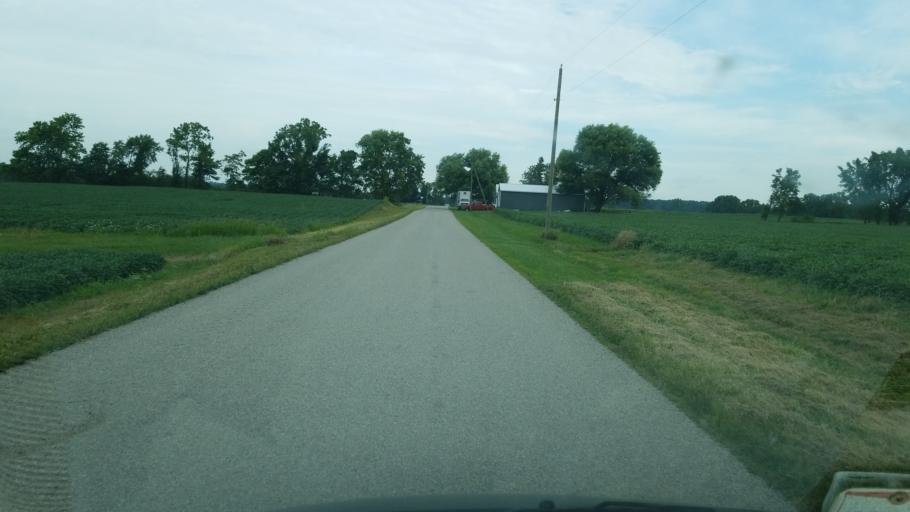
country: US
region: Ohio
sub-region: Seneca County
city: Tiffin
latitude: 41.0290
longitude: -83.0546
